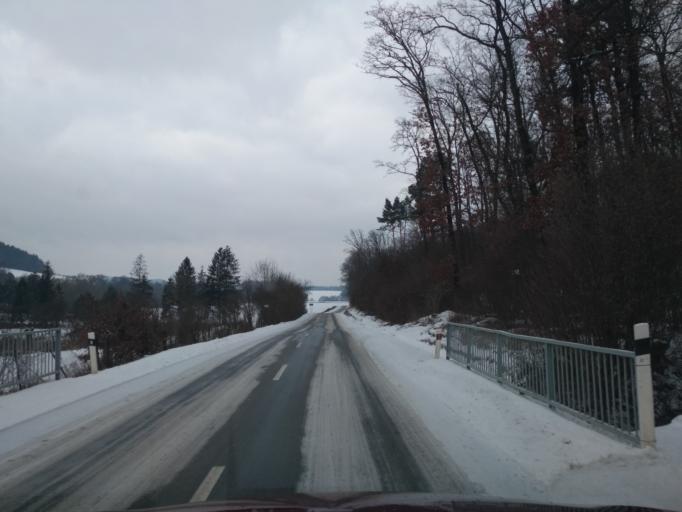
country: SK
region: Presovsky
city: Sabinov
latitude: 49.0393
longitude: 21.0998
